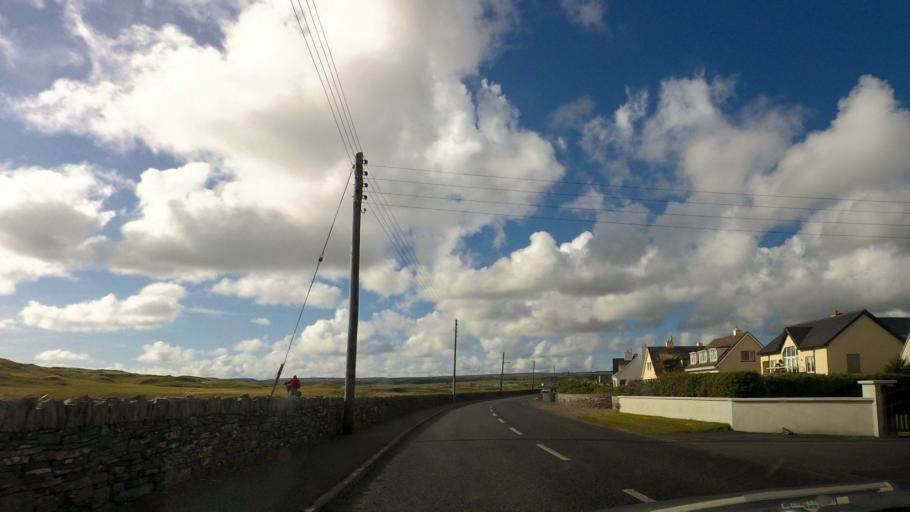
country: IE
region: Munster
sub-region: An Clar
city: Kilrush
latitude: 52.9380
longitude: -9.3468
